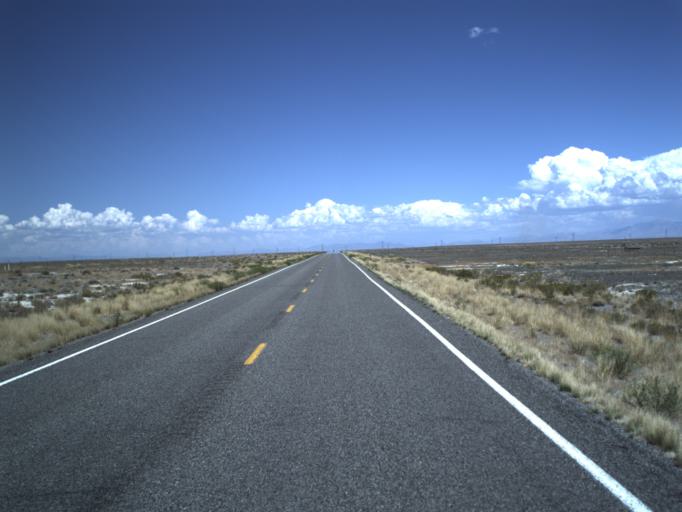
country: US
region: Utah
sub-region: Millard County
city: Delta
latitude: 39.2158
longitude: -112.9567
